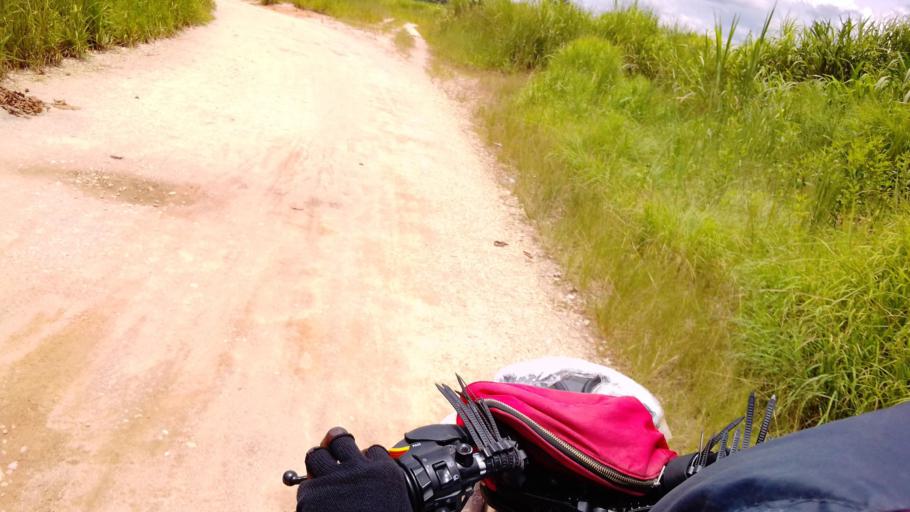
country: SL
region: Eastern Province
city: Koidu
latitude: 8.6736
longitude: -10.9564
